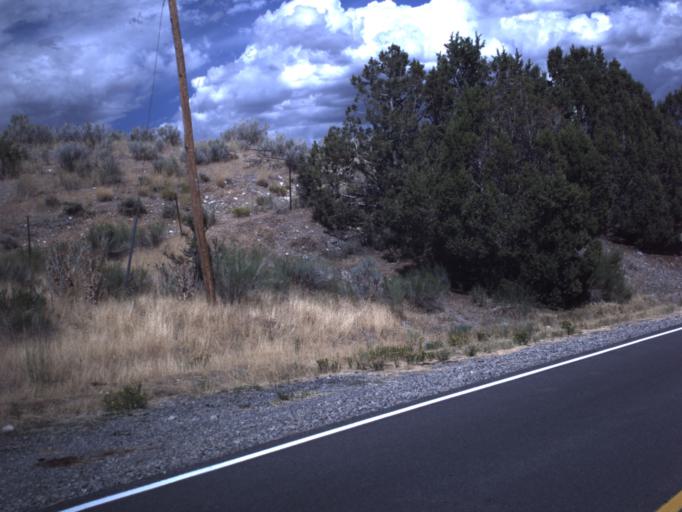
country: US
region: Utah
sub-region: Tooele County
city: Grantsville
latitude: 40.3418
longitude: -112.5397
